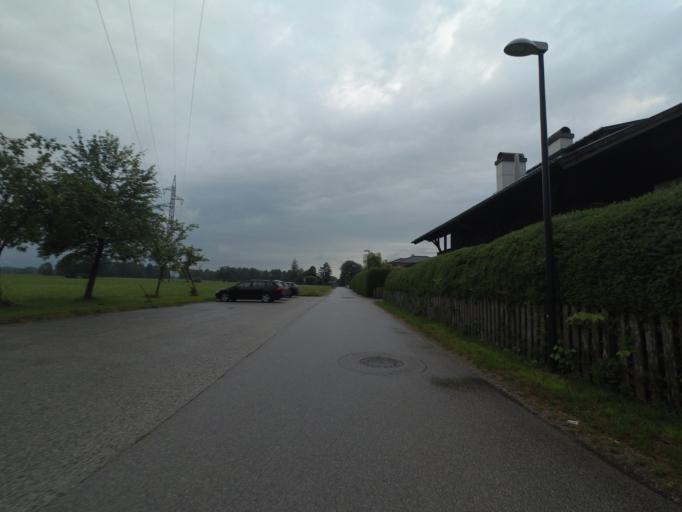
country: AT
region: Salzburg
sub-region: Politischer Bezirk Salzburg-Umgebung
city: Grodig
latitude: 47.7552
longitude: 13.0340
